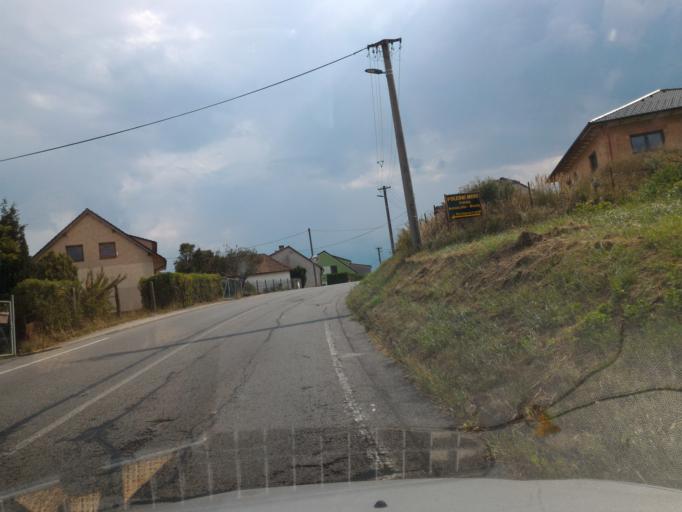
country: CZ
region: Vysocina
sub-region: Okres Jihlava
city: Trest'
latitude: 49.2752
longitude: 15.4747
